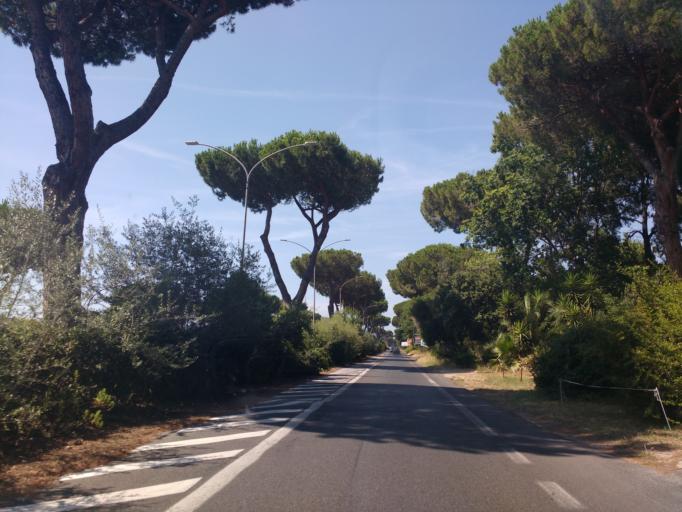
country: IT
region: Latium
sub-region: Citta metropolitana di Roma Capitale
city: Acilia-Castel Fusano-Ostia Antica
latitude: 41.7480
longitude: 12.3606
